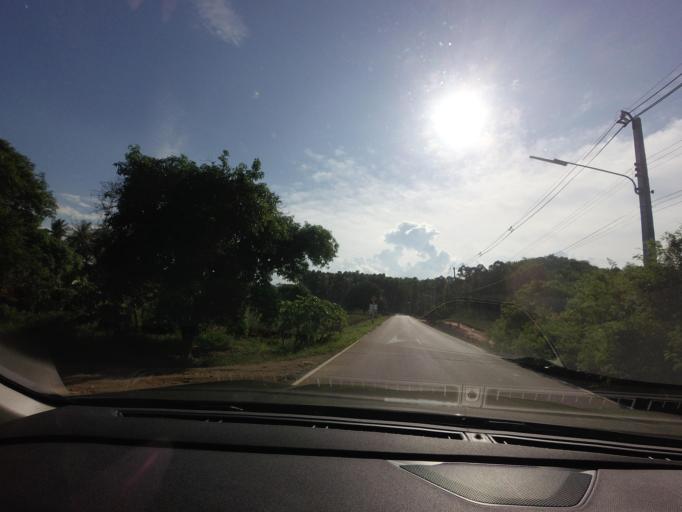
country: TH
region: Prachuap Khiri Khan
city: Pran Buri
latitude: 12.4125
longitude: 99.9676
